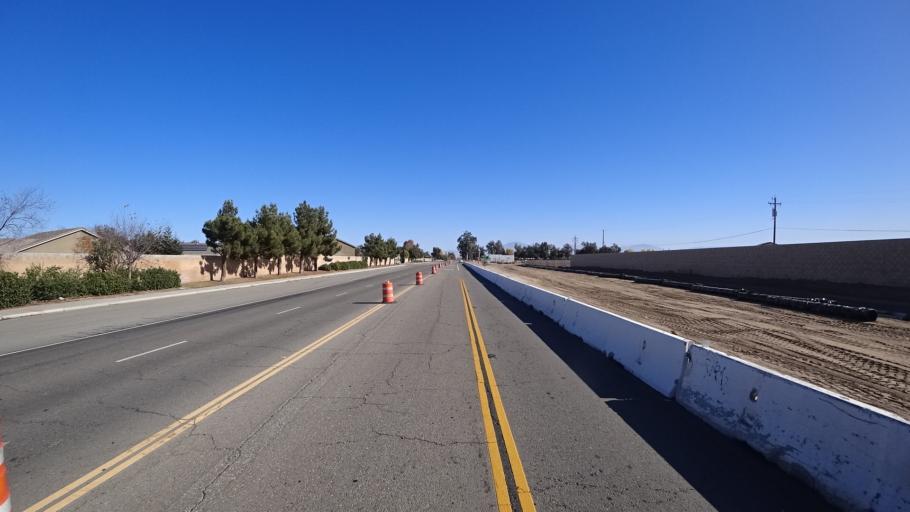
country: US
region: California
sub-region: Kern County
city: Greenfield
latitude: 35.2670
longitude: -119.0674
